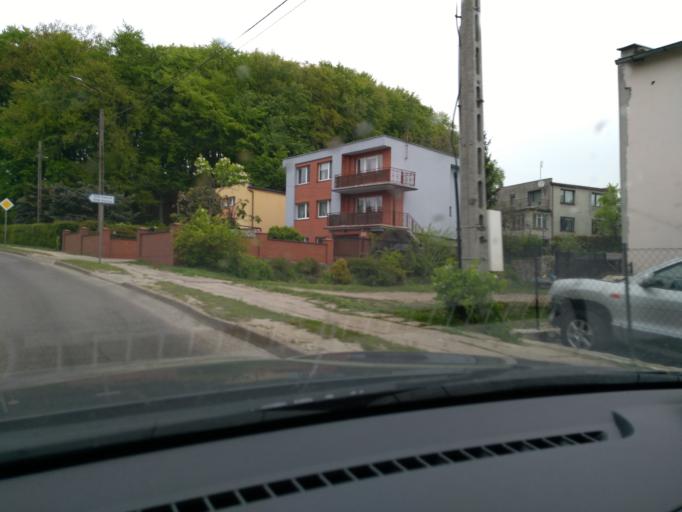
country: PL
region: Pomeranian Voivodeship
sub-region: Powiat kartuski
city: Kartuzy
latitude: 54.3381
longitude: 18.1864
